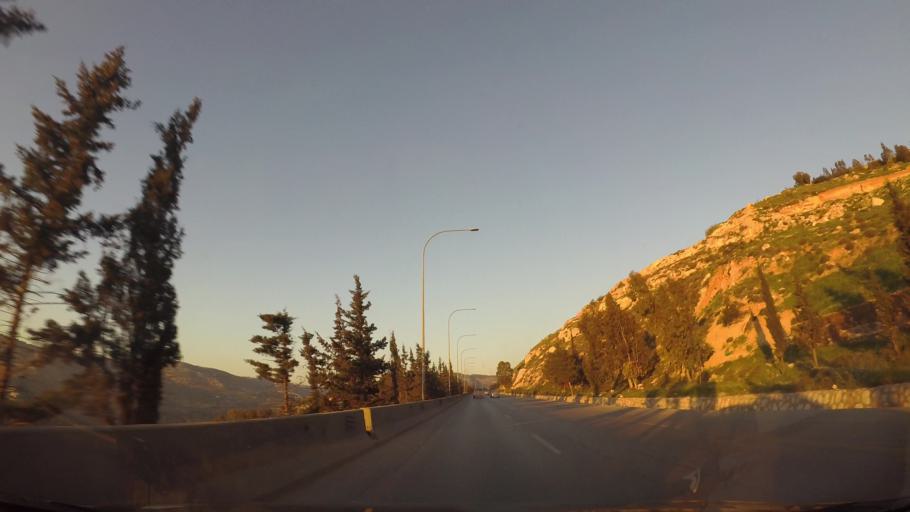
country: JO
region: Amman
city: Umm as Summaq
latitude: 31.8785
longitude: 35.7825
